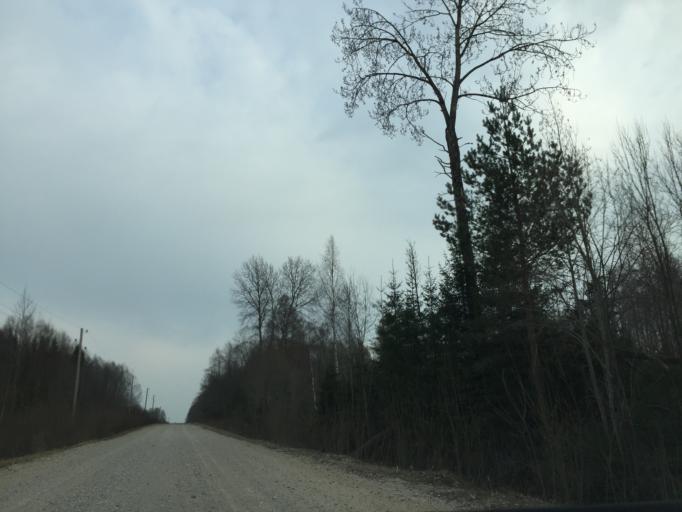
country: LV
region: Priekuli
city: Priekuli
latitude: 57.1828
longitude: 25.4694
